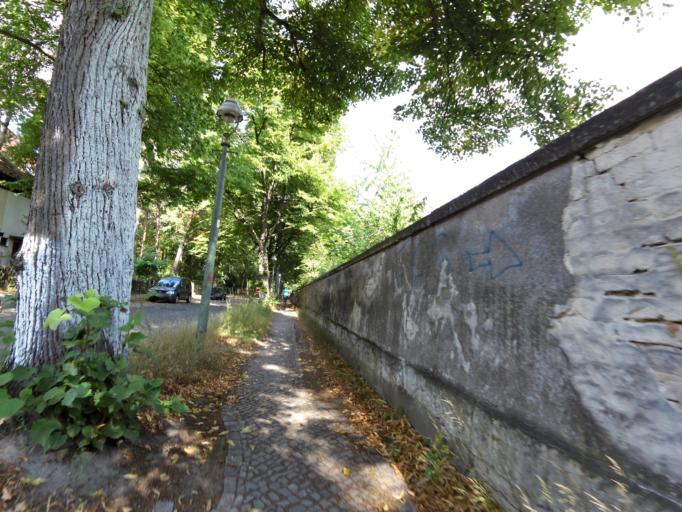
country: DE
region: Berlin
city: Lichtenrade
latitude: 52.3801
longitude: 13.3989
